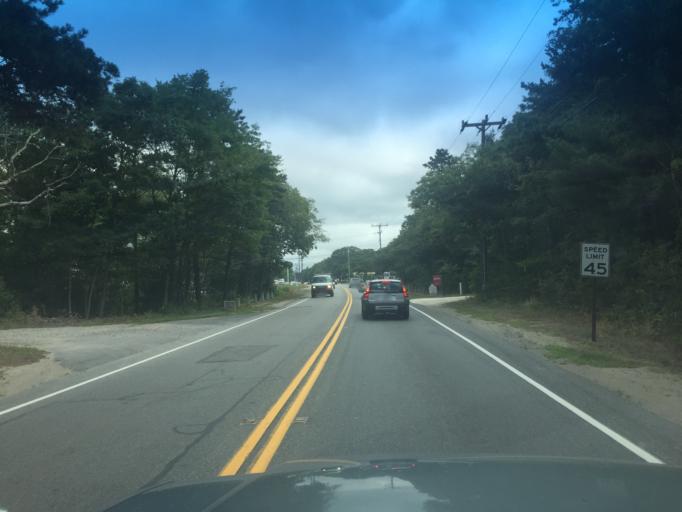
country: US
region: Massachusetts
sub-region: Barnstable County
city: Mashpee
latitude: 41.6157
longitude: -70.5215
